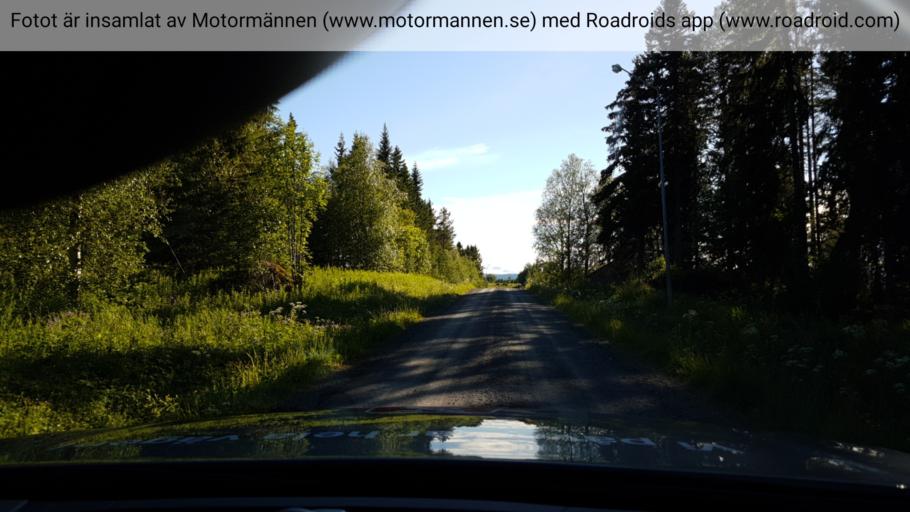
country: SE
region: Jaemtland
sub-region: Bergs Kommun
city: Hoverberg
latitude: 63.0273
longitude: 14.3826
